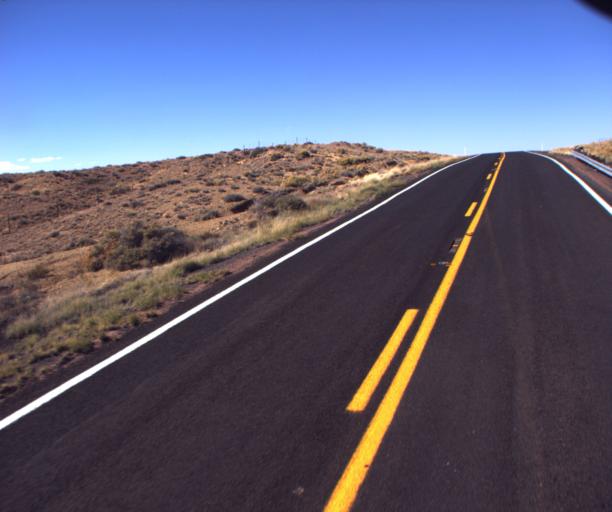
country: US
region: Arizona
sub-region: Coconino County
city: Tuba City
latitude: 35.9578
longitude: -110.9331
